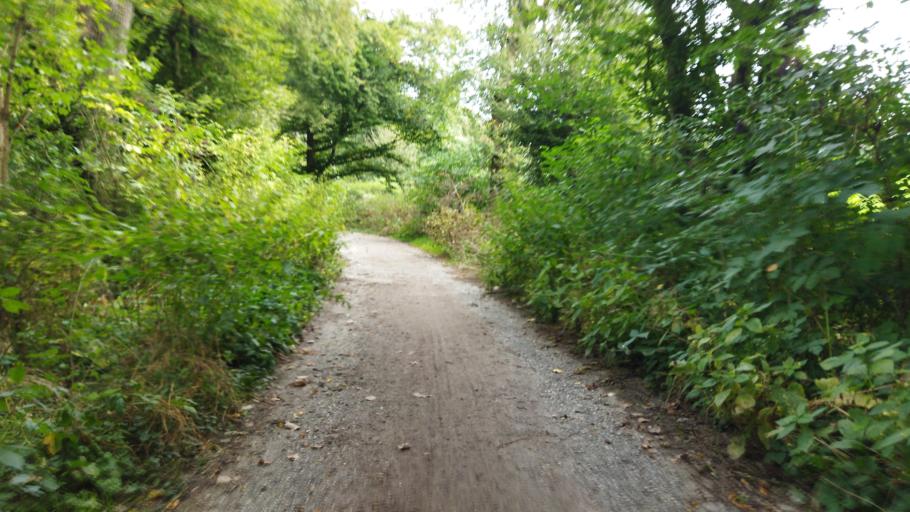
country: DE
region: Lower Saxony
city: Bad Rothenfelde
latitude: 52.1184
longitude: 8.1568
